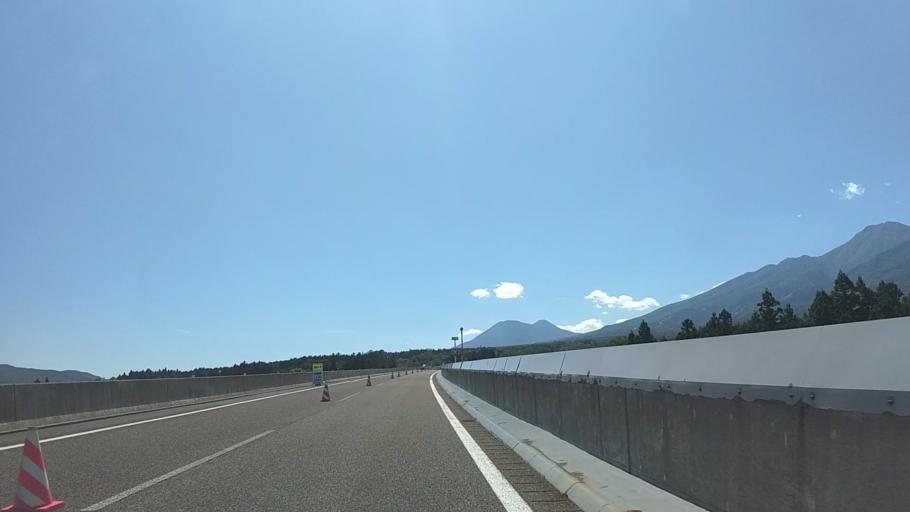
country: JP
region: Niigata
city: Arai
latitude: 36.9495
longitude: 138.2164
